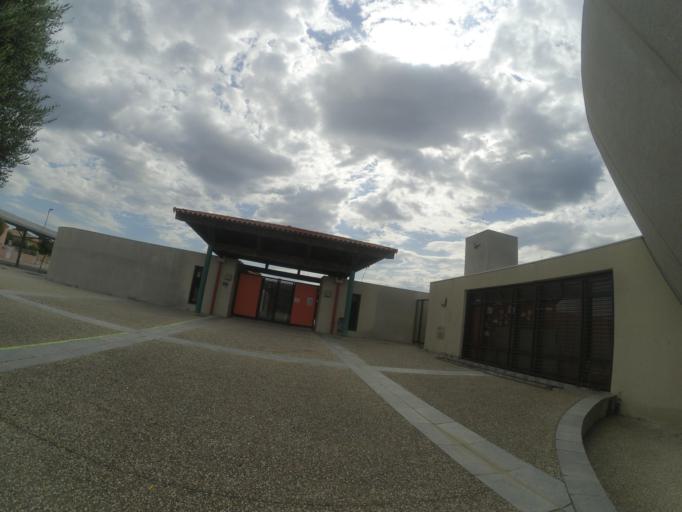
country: FR
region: Languedoc-Roussillon
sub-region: Departement des Pyrenees-Orientales
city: Villeneuve-la-Riviere
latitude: 42.6810
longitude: 2.8071
